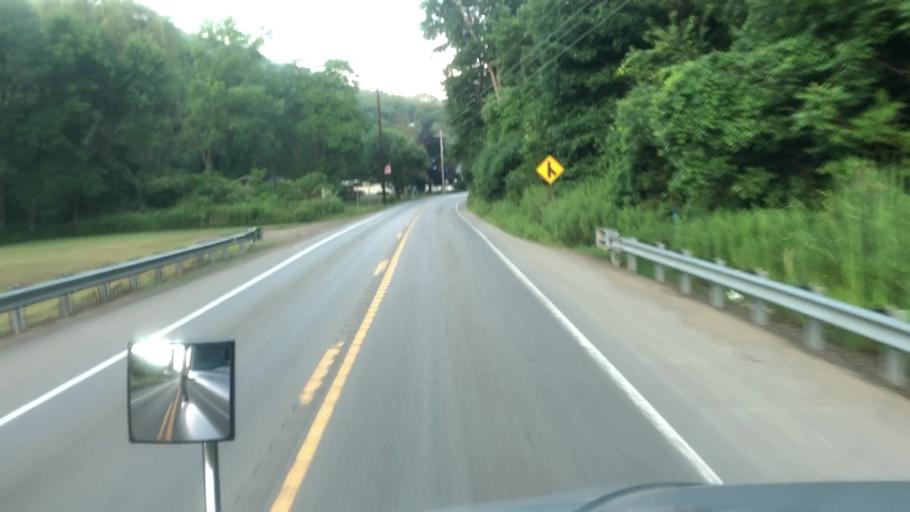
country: US
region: Pennsylvania
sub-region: Venango County
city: Hasson Heights
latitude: 41.4733
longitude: -79.6835
